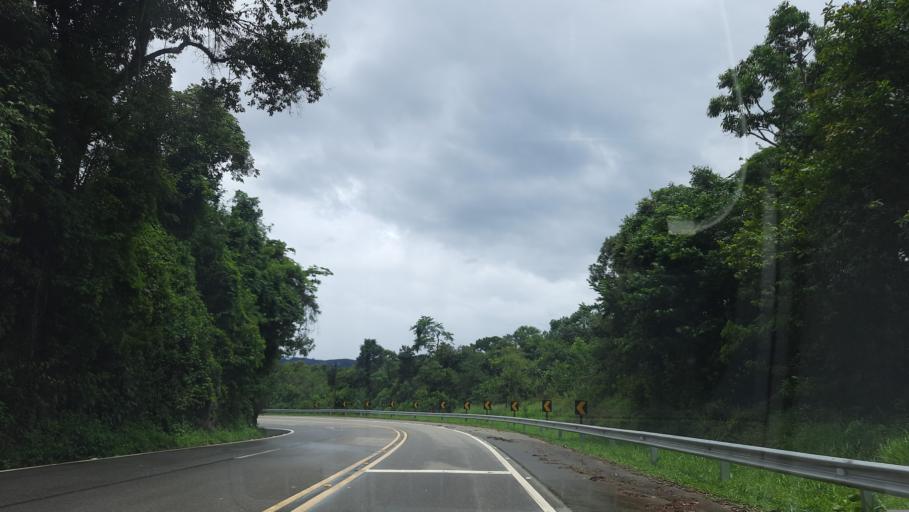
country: BR
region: Minas Gerais
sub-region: Pocos De Caldas
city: Pocos de Caldas
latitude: -21.8462
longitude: -46.6907
